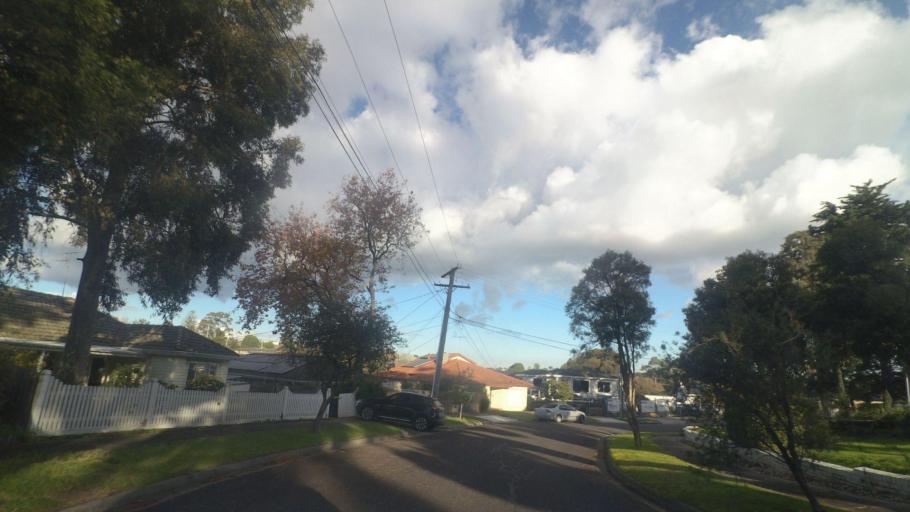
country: AU
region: Victoria
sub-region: Boroondara
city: Balwyn North
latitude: -37.7808
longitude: 145.1011
